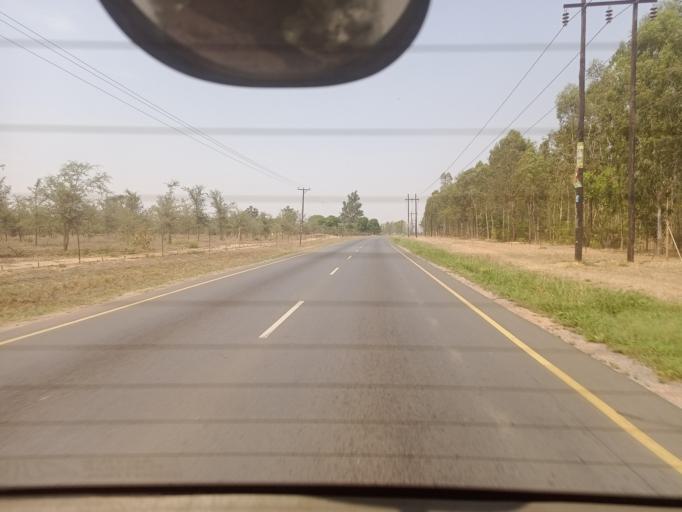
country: ZM
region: Lusaka
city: Lusaka
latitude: -15.2867
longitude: 28.3804
